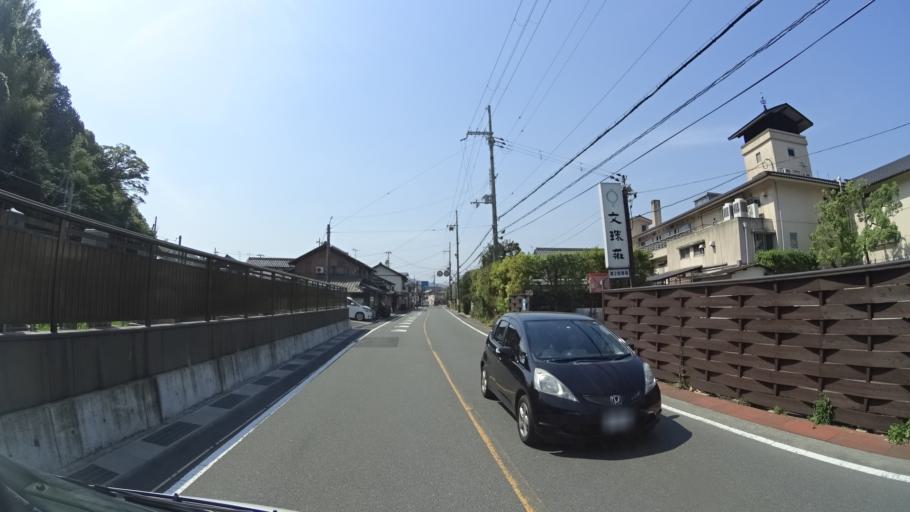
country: JP
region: Kyoto
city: Miyazu
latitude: 35.5555
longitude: 135.1861
